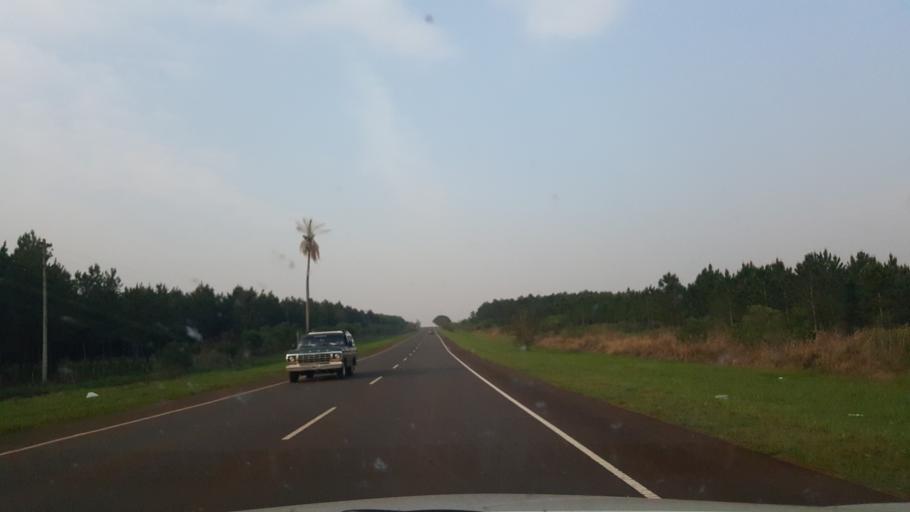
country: AR
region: Misiones
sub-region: Departamento de Capital
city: Posadas
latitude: -27.4307
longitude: -56.0069
